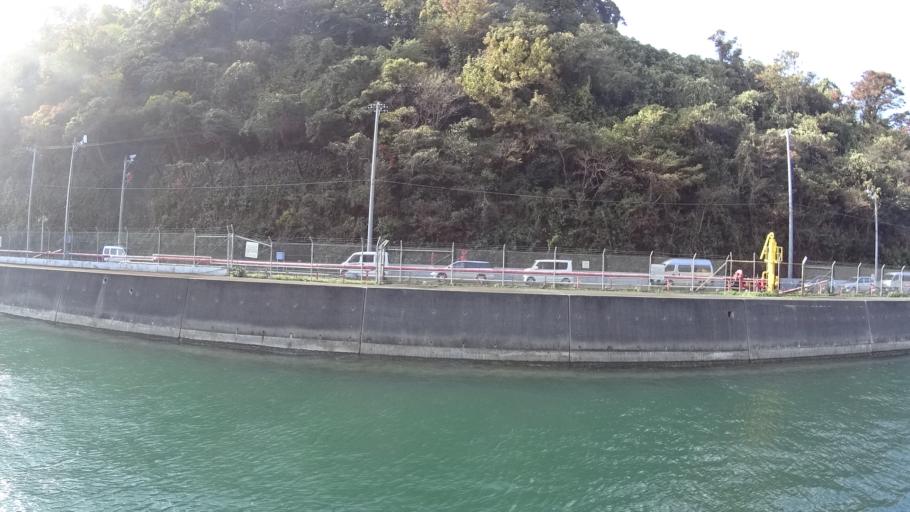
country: JP
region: Kanagawa
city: Yokosuka
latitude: 35.2964
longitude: 139.6464
